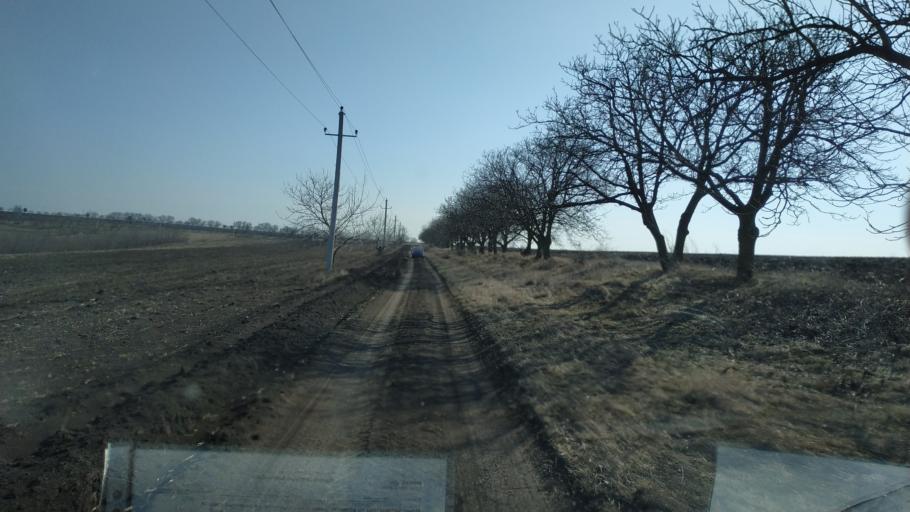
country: MD
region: Causeni
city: Causeni
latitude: 46.5560
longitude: 29.2691
